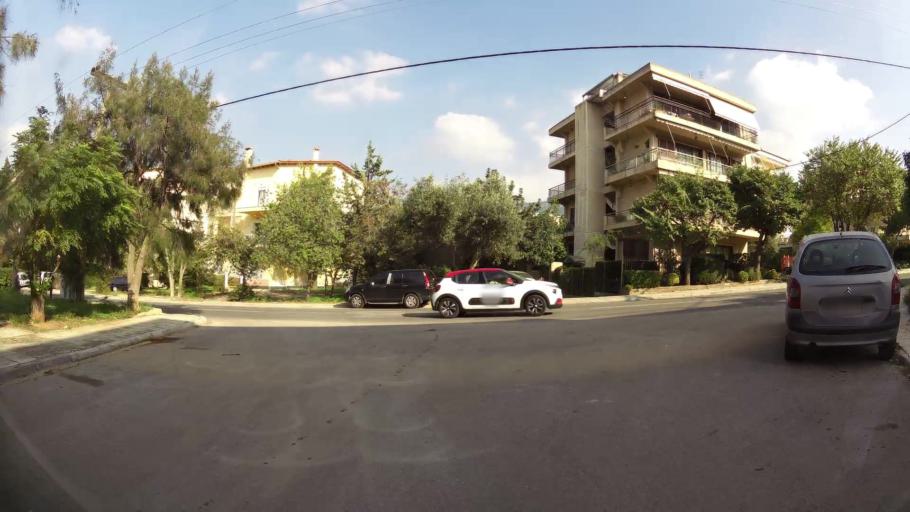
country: GR
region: Attica
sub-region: Nomarchia Athinas
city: Papagou
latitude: 37.9817
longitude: 23.7964
